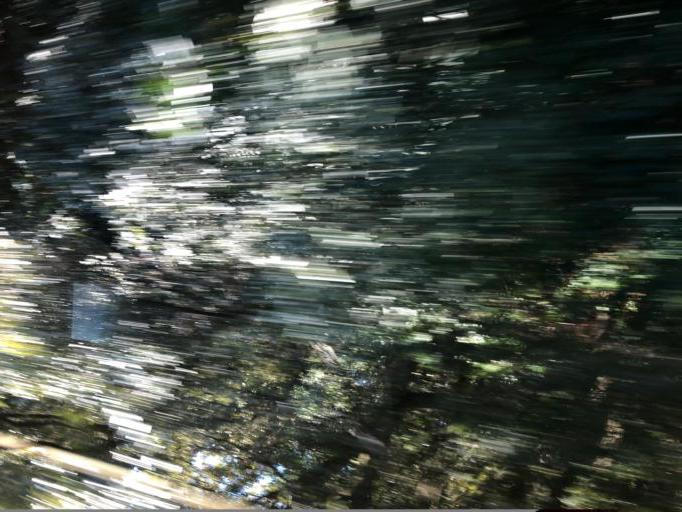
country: JP
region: Kochi
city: Nakamura
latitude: 33.0372
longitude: 133.0225
